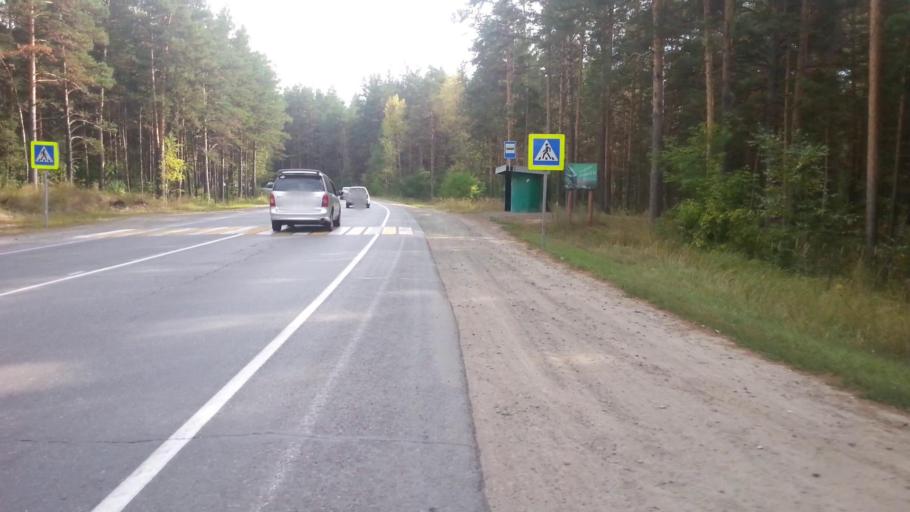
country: RU
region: Altai Krai
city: Yuzhnyy
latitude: 53.2994
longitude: 83.7028
